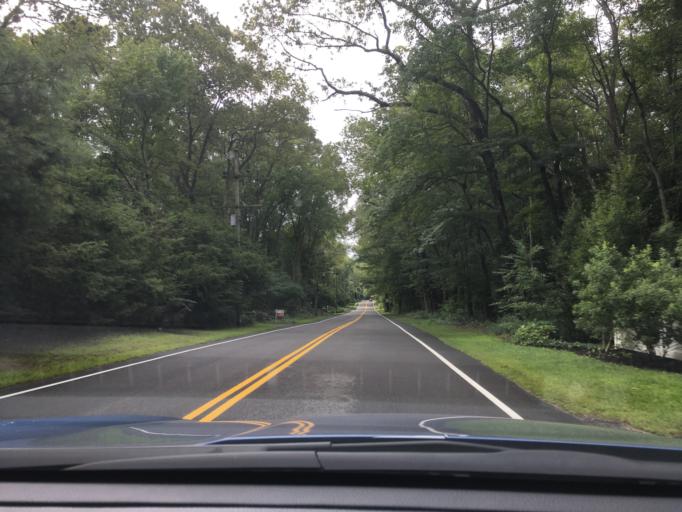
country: US
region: Rhode Island
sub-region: Kent County
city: East Greenwich
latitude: 41.6547
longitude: -71.4754
